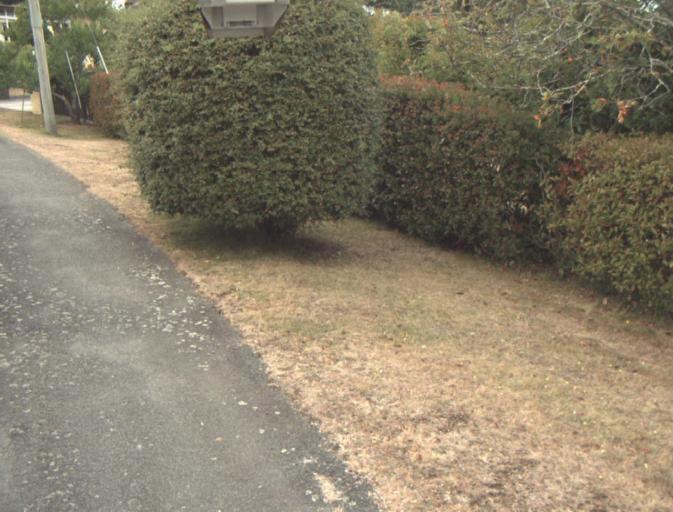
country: AU
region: Tasmania
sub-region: Launceston
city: Mayfield
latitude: -41.3302
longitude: 147.0669
